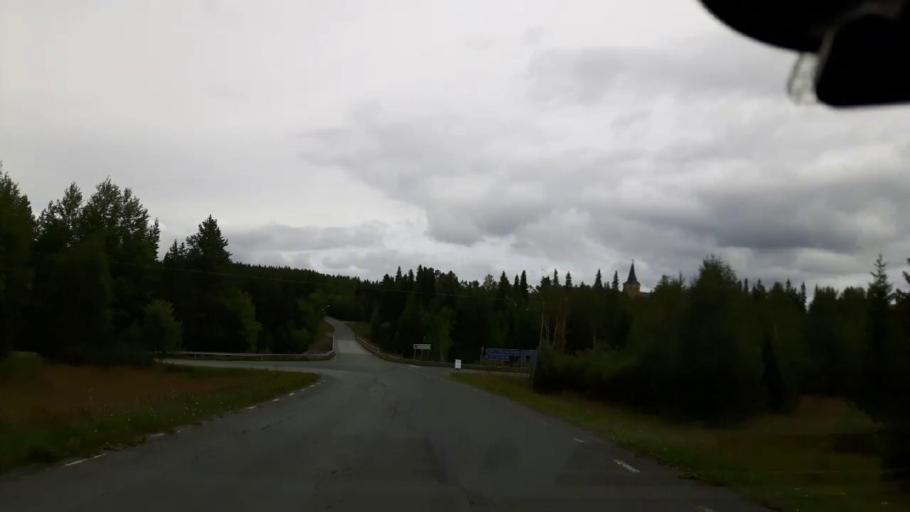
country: SE
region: Jaemtland
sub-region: Krokoms Kommun
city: Valla
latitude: 63.6450
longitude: 13.8282
